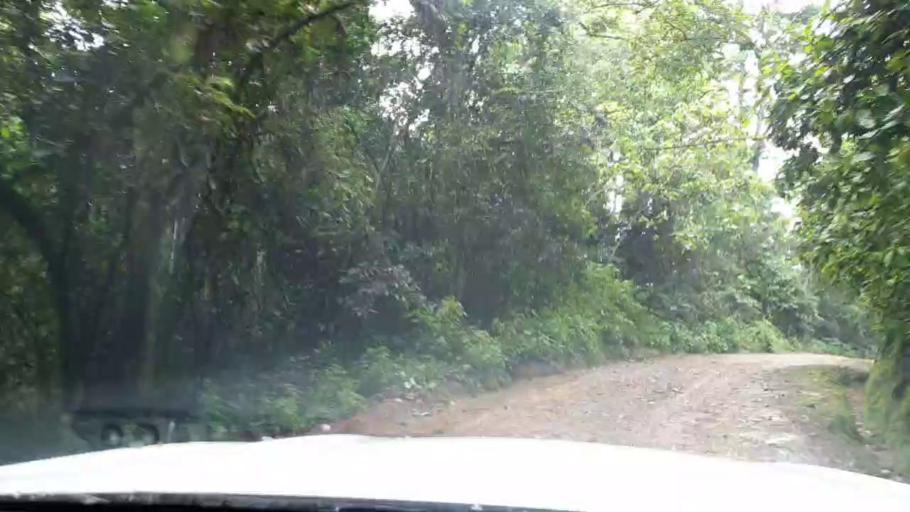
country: RW
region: Western Province
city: Cyangugu
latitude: -2.5587
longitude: 28.9831
